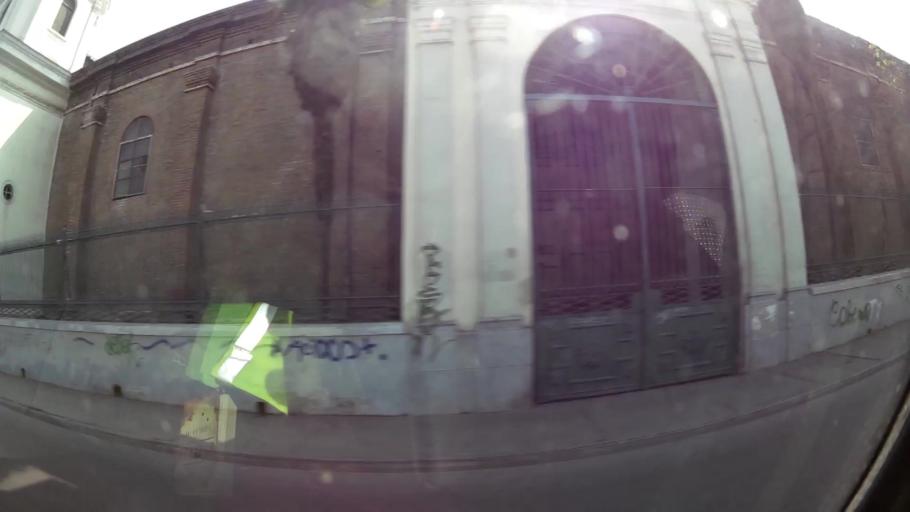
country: CL
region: Santiago Metropolitan
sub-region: Provincia de Santiago
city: Santiago
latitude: -33.4556
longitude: -70.6508
